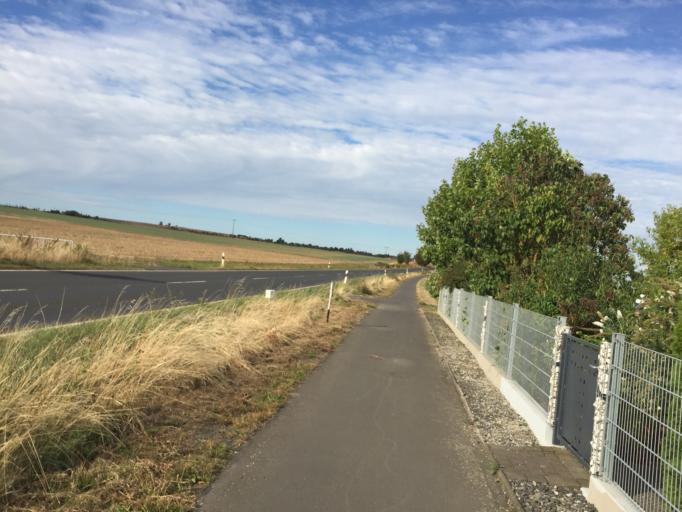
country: DE
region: Hesse
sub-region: Regierungsbezirk Giessen
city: Langgons
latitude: 50.4937
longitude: 8.7229
